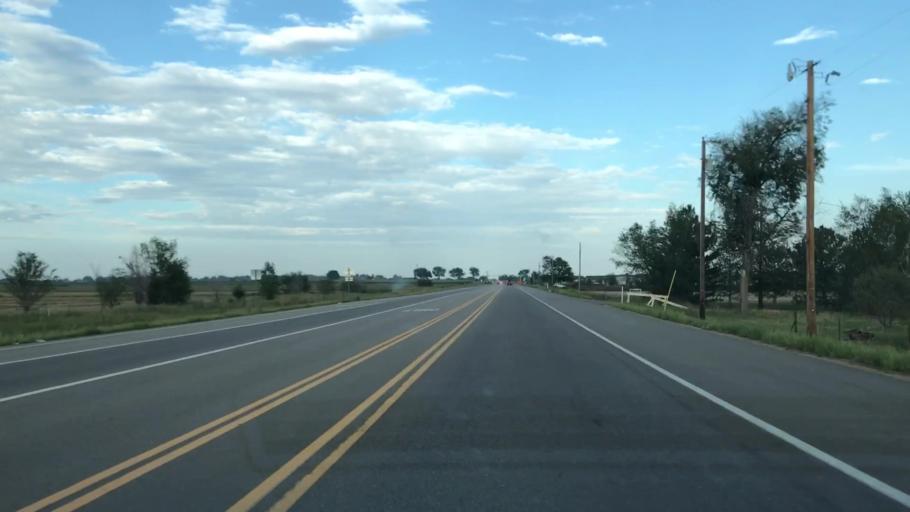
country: US
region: Colorado
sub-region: Boulder County
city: Longmont
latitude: 40.2032
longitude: -105.0828
